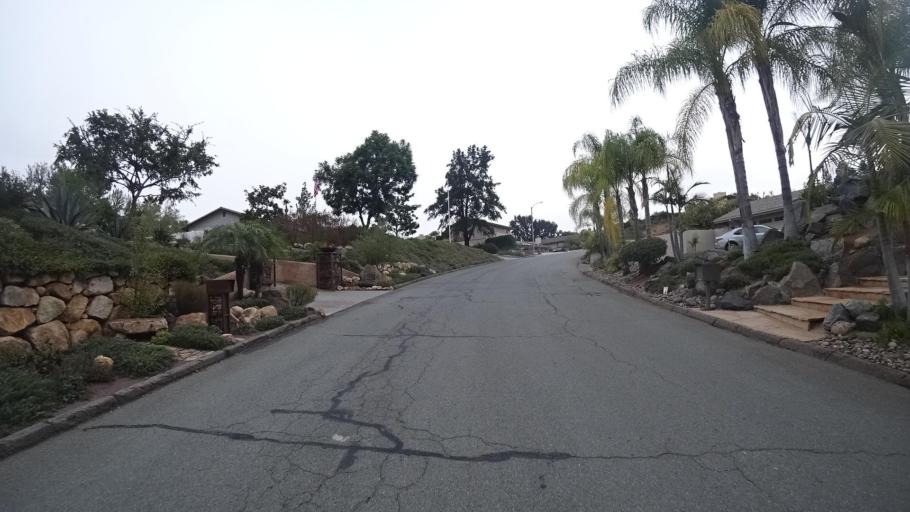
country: US
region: California
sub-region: San Diego County
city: Granite Hills
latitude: 32.7749
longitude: -116.9157
